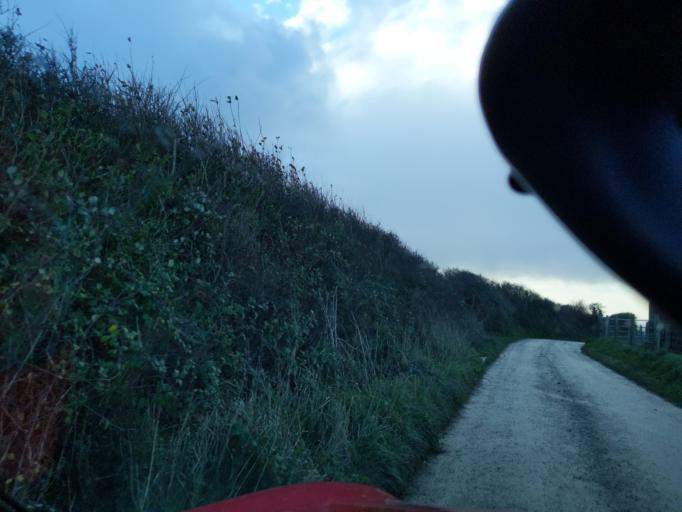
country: GB
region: England
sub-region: Cornwall
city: Looe
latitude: 50.3405
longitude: -4.4819
